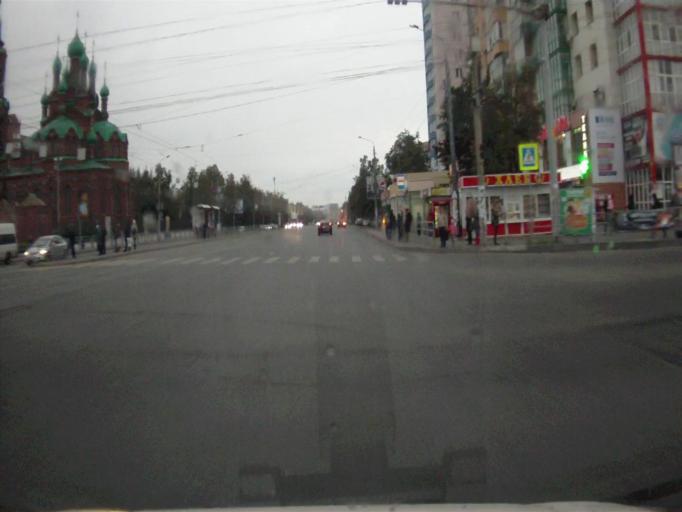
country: RU
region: Chelyabinsk
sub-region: Gorod Chelyabinsk
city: Chelyabinsk
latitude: 55.1733
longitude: 61.4000
